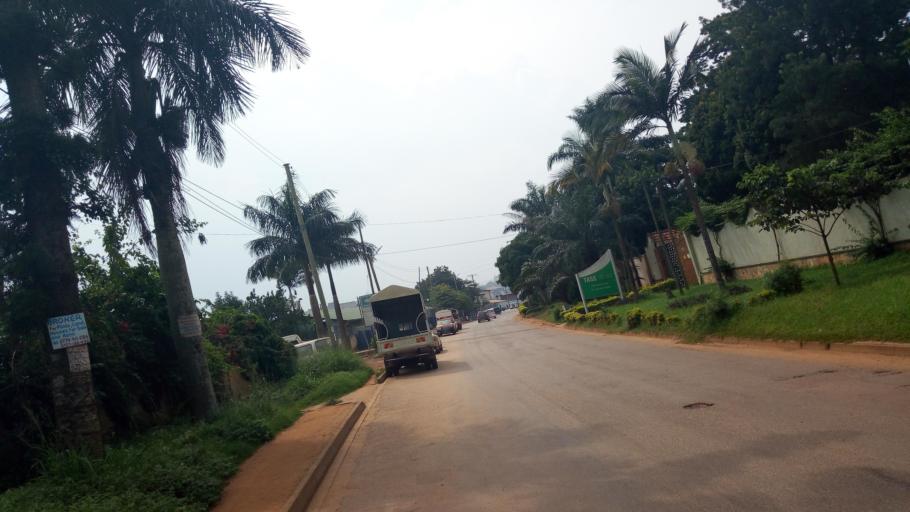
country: UG
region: Central Region
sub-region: Kampala District
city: Kampala
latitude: 0.3125
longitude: 32.6177
